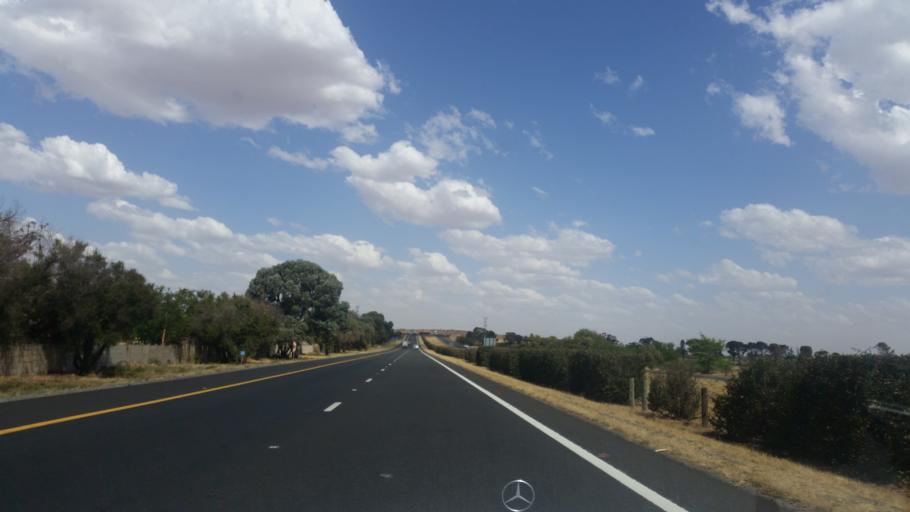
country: ZA
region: Orange Free State
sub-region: Mangaung Metropolitan Municipality
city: Bloemfontein
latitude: -29.1733
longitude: 26.1860
